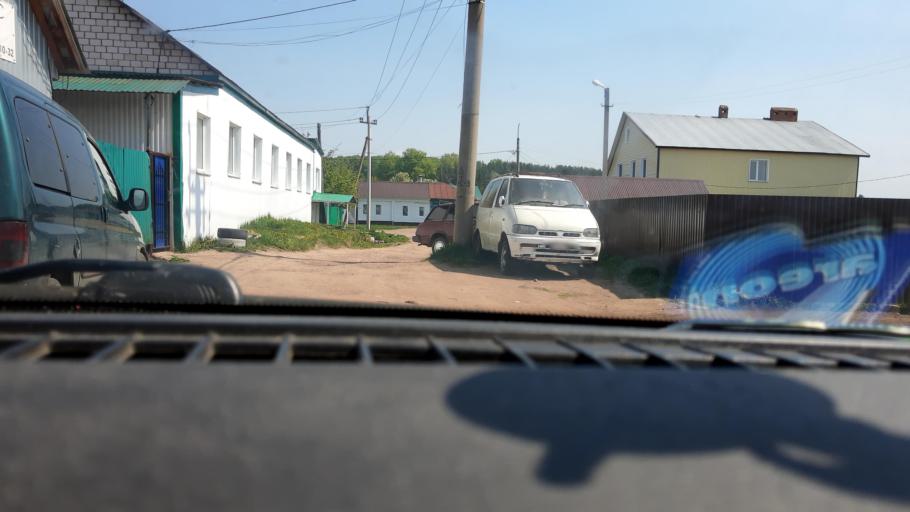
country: RU
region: Bashkortostan
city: Blagoveshchensk
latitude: 55.0225
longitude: 55.9829
